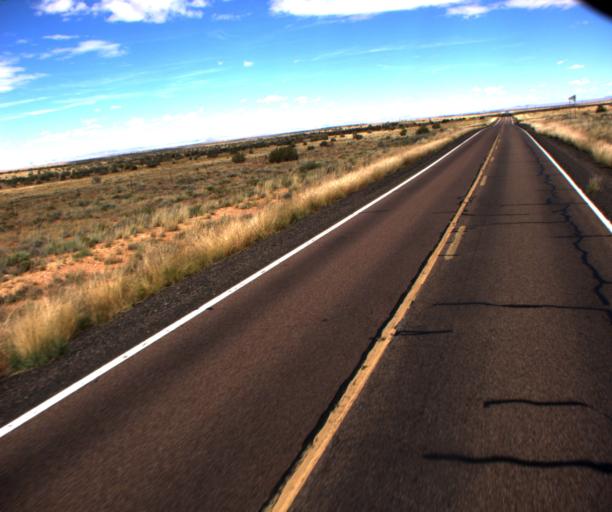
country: US
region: Arizona
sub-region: Navajo County
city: Holbrook
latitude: 34.7578
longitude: -110.2508
